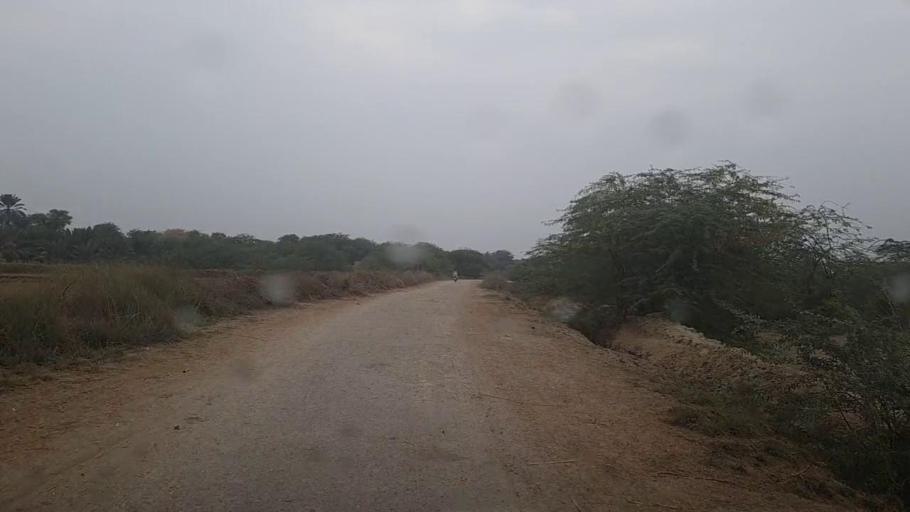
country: PK
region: Sindh
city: Gambat
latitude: 27.3439
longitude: 68.6019
